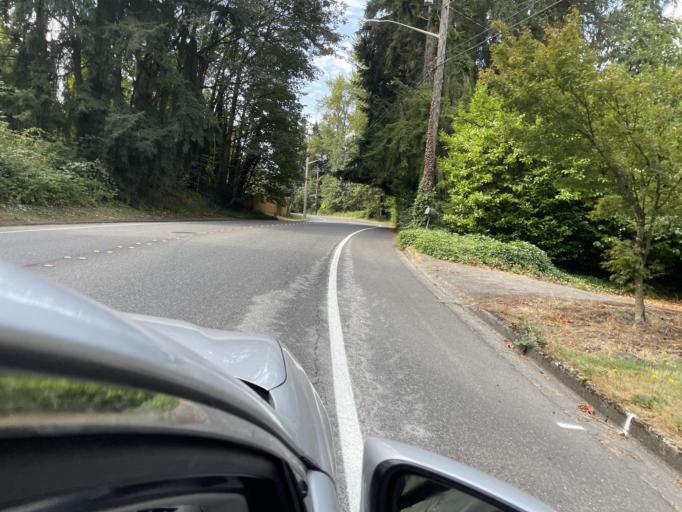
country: US
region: Washington
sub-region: King County
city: Eastgate
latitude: 47.5671
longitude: -122.1423
